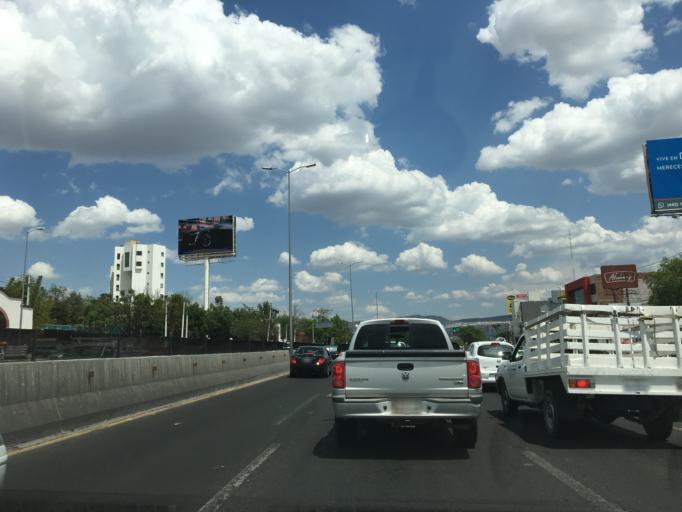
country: MX
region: Queretaro
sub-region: Queretaro
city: Santiago de Queretaro
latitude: 20.6080
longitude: -100.3789
